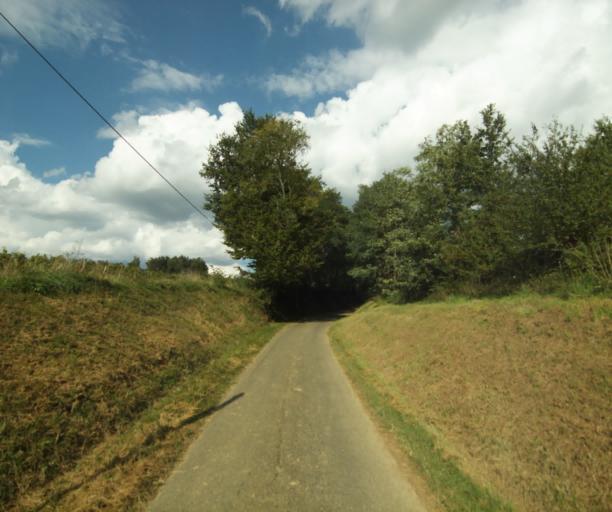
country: FR
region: Midi-Pyrenees
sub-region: Departement du Gers
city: Cazaubon
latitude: 43.9241
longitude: -0.0483
